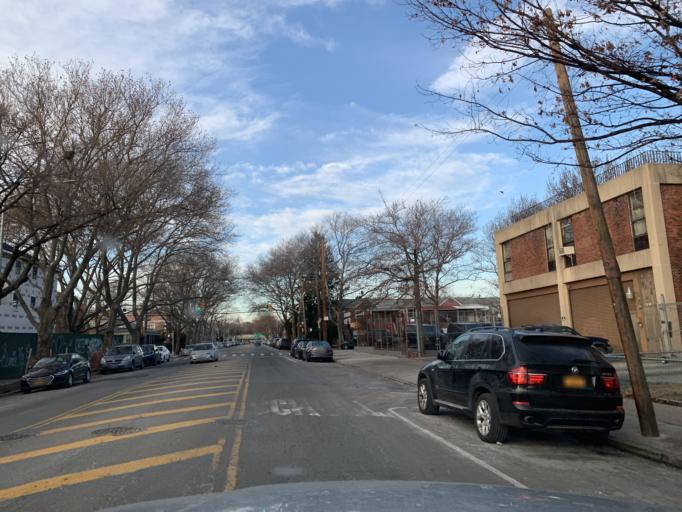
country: US
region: New York
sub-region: Queens County
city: Long Island City
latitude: 40.7604
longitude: -73.8940
